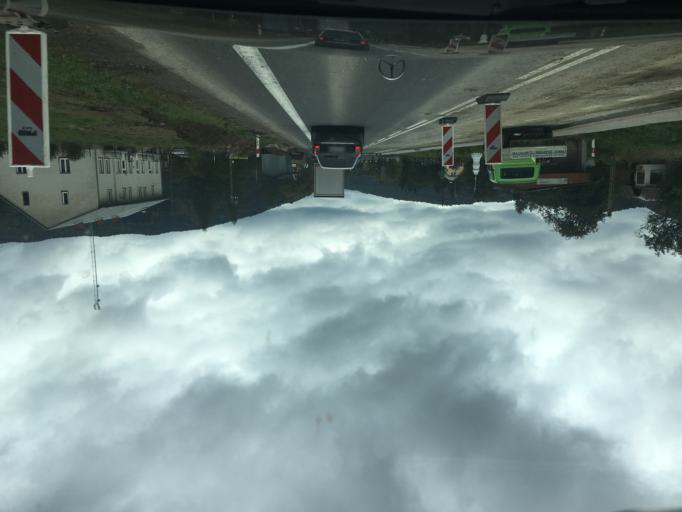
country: PL
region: Subcarpathian Voivodeship
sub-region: Powiat krosnienski
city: Dukla
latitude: 49.5034
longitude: 21.6986
